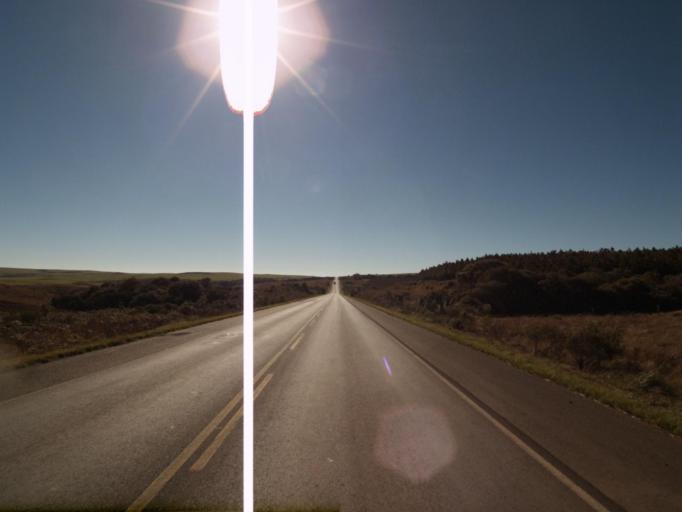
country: BR
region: Parana
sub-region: Palmas
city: Palmas
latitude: -26.7424
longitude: -51.6562
